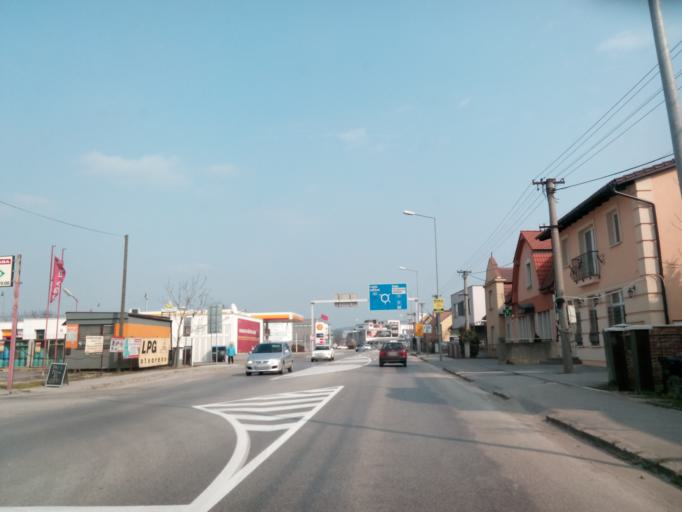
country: SK
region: Trenciansky
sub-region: Okres Trencin
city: Trencin
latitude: 48.9001
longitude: 18.0255
